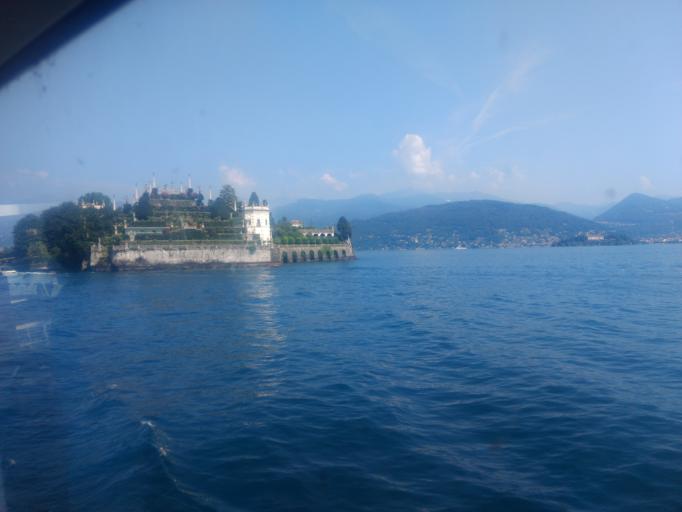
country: IT
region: Piedmont
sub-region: Provincia Verbano-Cusio-Ossola
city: Stresa
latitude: 45.8927
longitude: 8.5292
